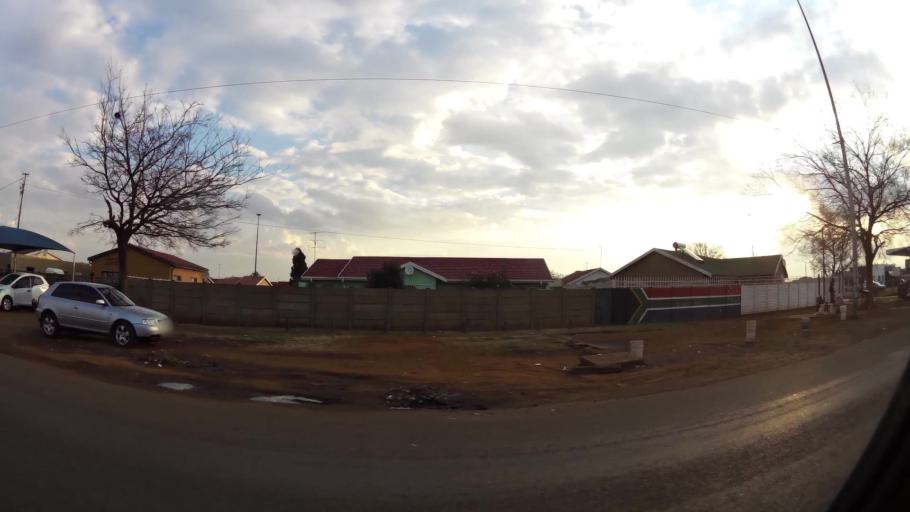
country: ZA
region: Gauteng
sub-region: City of Johannesburg Metropolitan Municipality
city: Orange Farm
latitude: -26.5887
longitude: 27.8465
